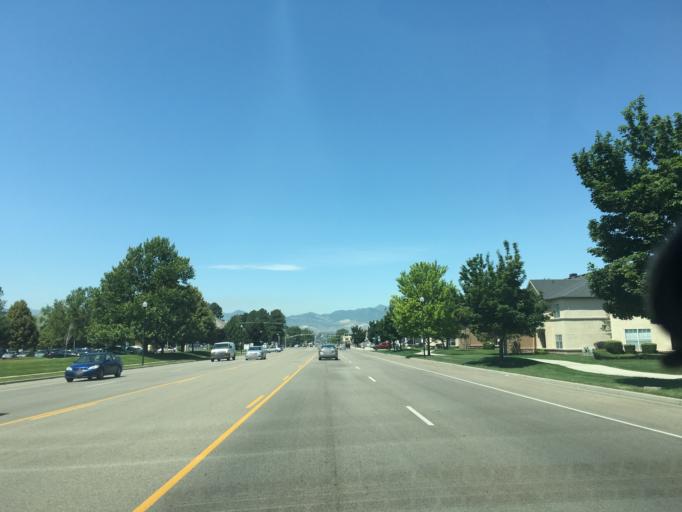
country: US
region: Utah
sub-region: Salt Lake County
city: Sandy City
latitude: 40.5880
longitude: -111.8685
